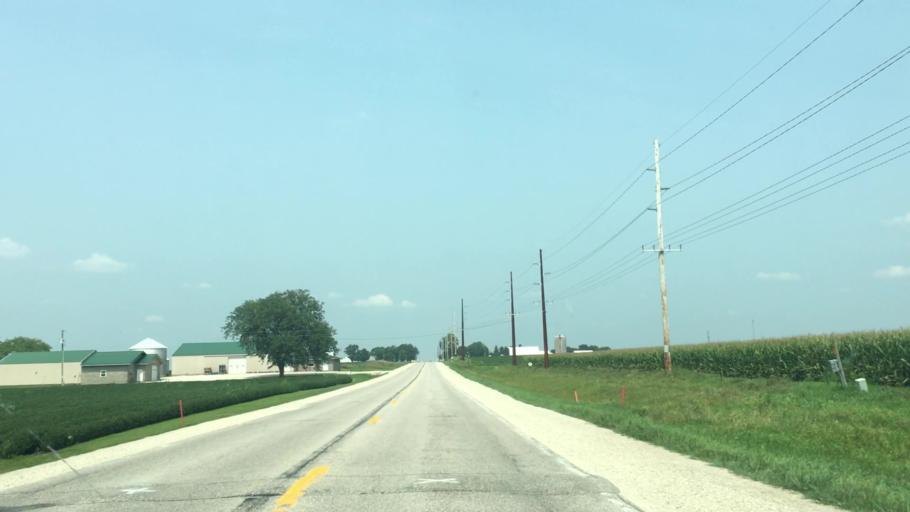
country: US
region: Iowa
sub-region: Buchanan County
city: Independence
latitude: 42.4347
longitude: -91.8899
